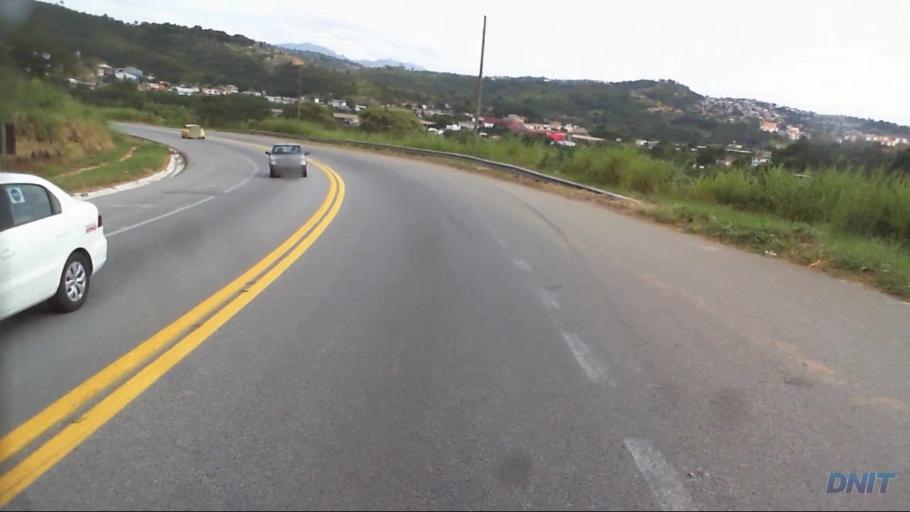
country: BR
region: Minas Gerais
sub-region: Santa Luzia
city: Santa Luzia
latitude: -19.8351
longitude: -43.8615
